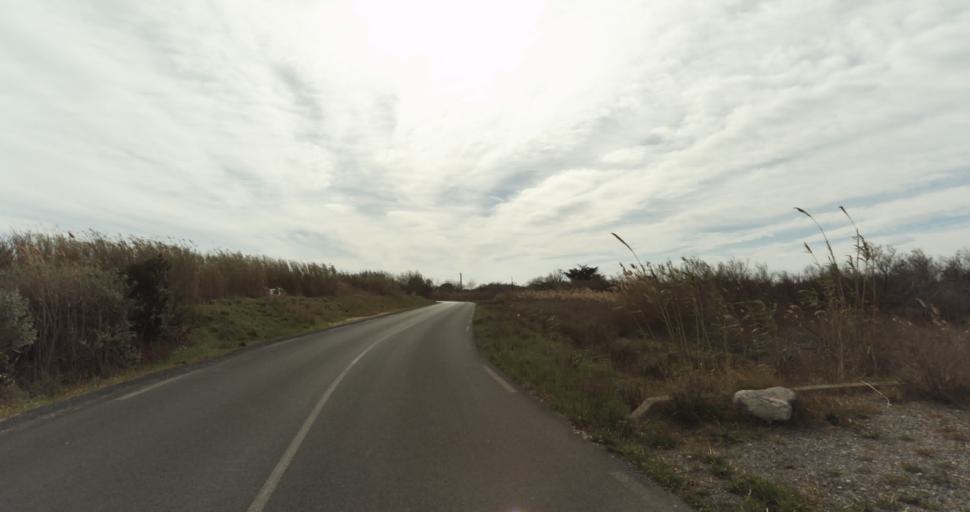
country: FR
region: Languedoc-Roussillon
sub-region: Departement de l'Herault
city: Marseillan
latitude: 43.3273
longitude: 3.5595
